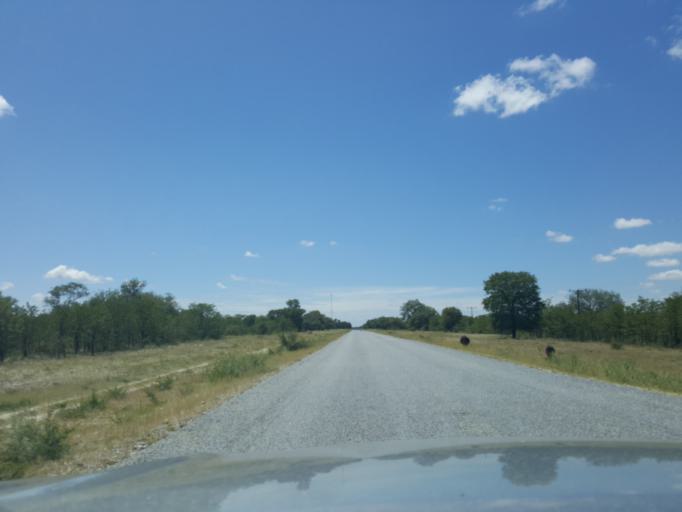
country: BW
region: Central
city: Nata
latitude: -20.1519
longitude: 25.7551
